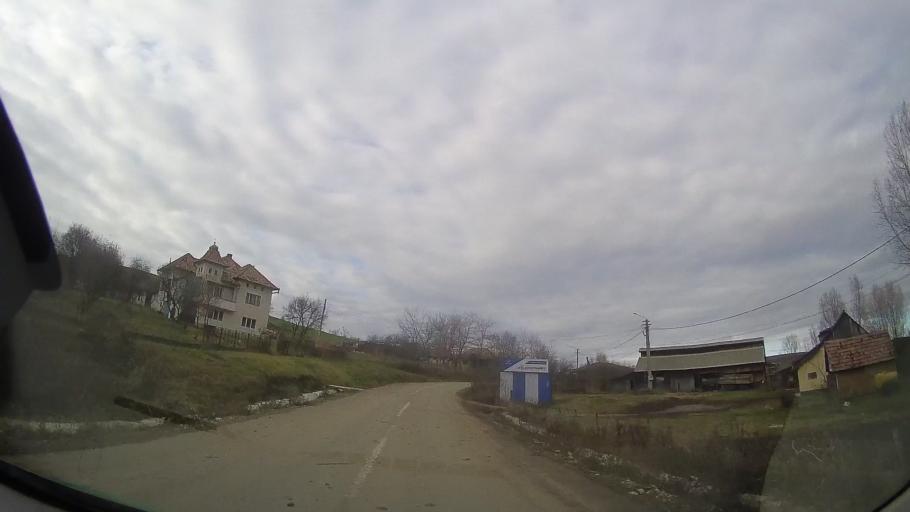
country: RO
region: Bistrita-Nasaud
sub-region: Comuna Micestii de Campie
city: Micestii de Campie
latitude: 46.8320
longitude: 24.3050
